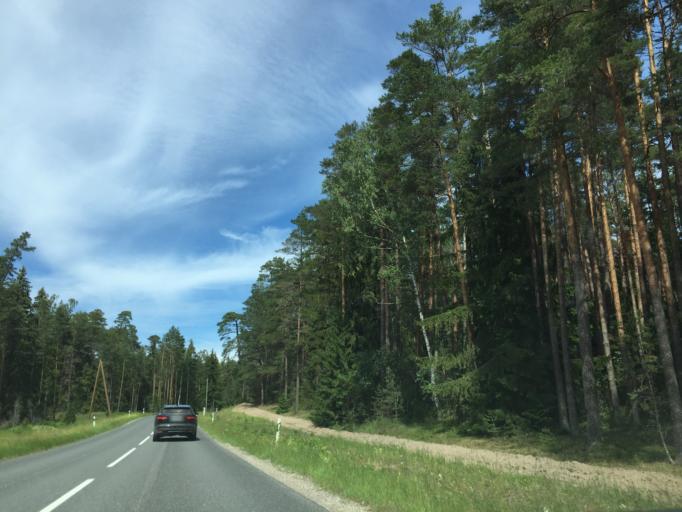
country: LV
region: Dundaga
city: Dundaga
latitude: 57.6389
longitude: 22.5667
